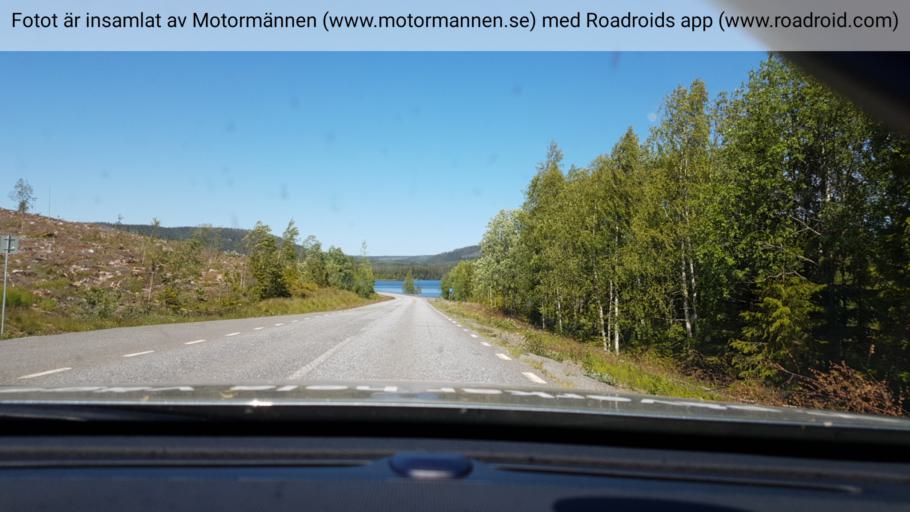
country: SE
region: Vaesterbotten
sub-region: Vilhelmina Kommun
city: Sjoberg
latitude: 64.9198
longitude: 15.8692
